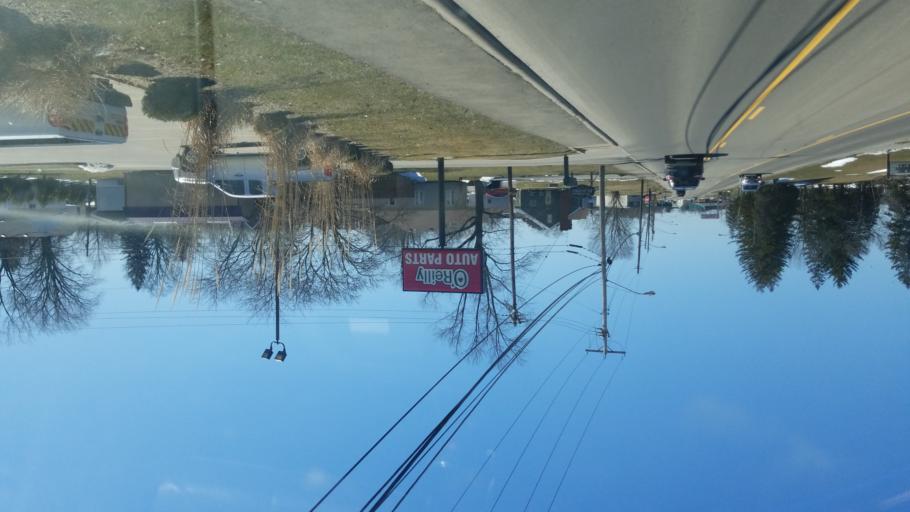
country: US
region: Ohio
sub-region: Crawford County
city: Bucyrus
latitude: 40.8114
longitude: -82.9573
